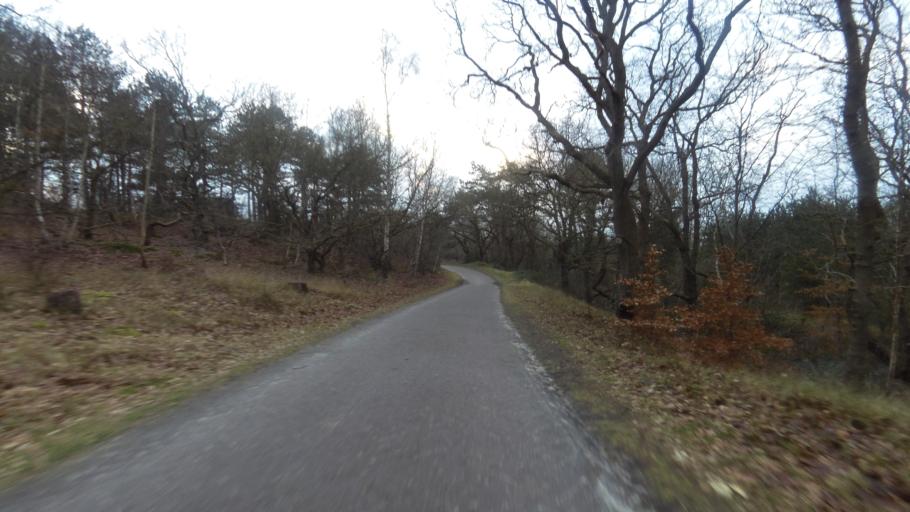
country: NL
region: North Holland
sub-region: Gemeente Alkmaar
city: Alkmaar
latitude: 52.6806
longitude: 4.6883
